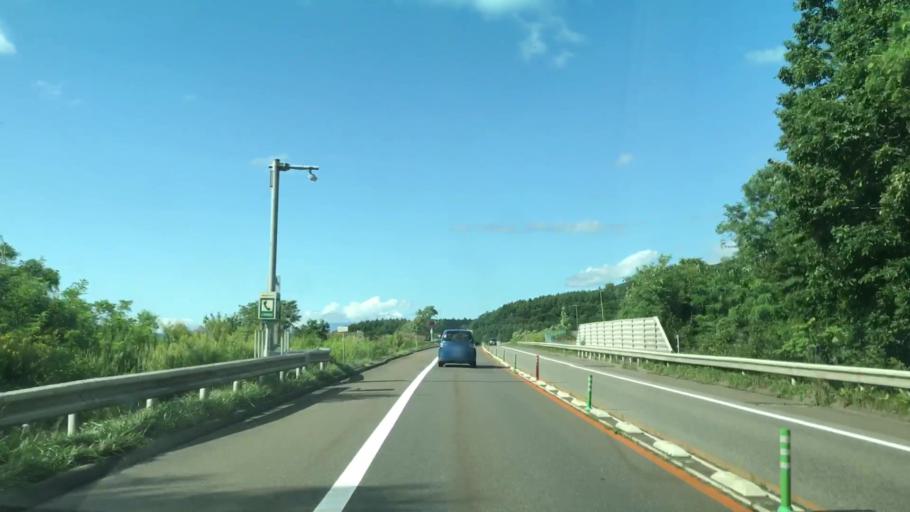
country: JP
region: Hokkaido
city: Date
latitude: 42.4492
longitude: 140.9135
